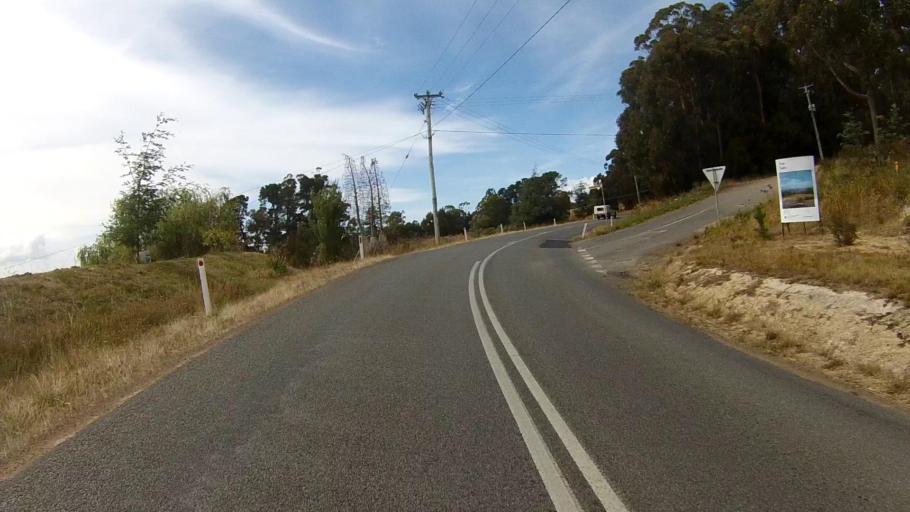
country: AU
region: Tasmania
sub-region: Kingborough
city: Kettering
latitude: -43.1919
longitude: 147.2472
